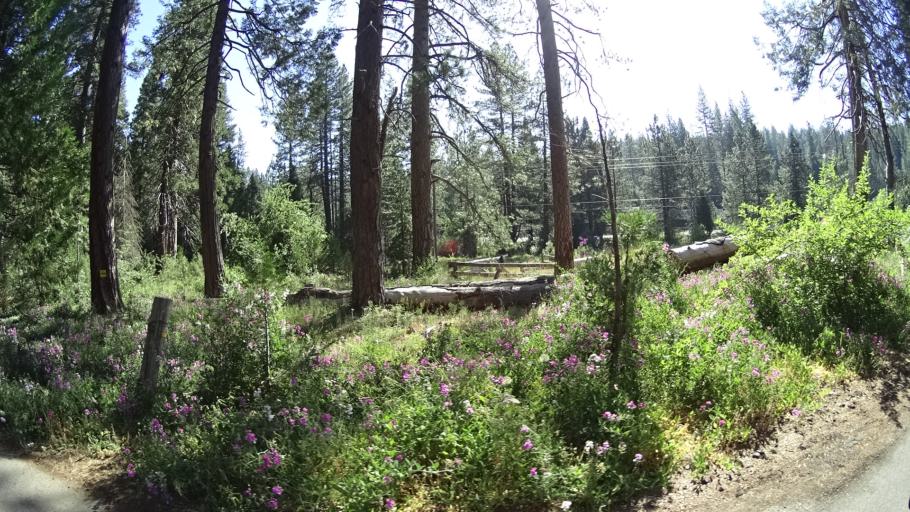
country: US
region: California
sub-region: Calaveras County
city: Arnold
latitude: 38.2643
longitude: -120.3446
